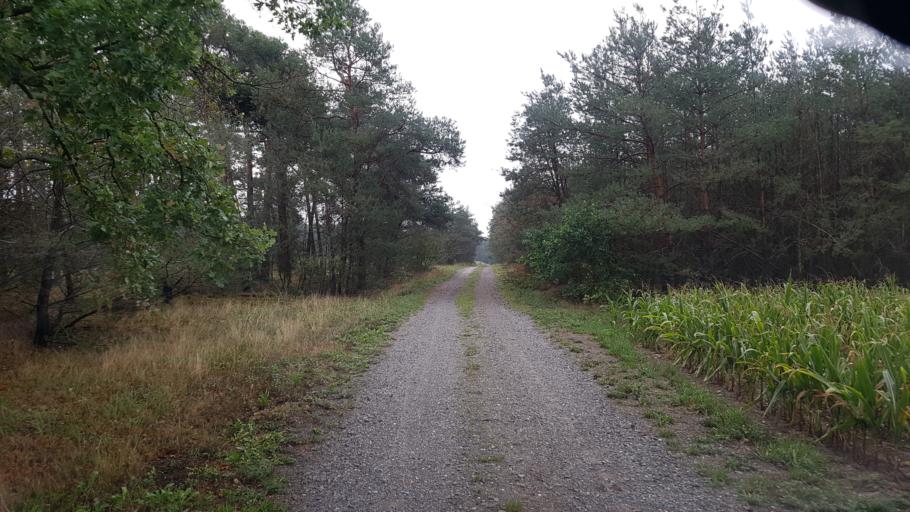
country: DE
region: Brandenburg
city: Ruckersdorf
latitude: 51.5673
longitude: 13.5633
